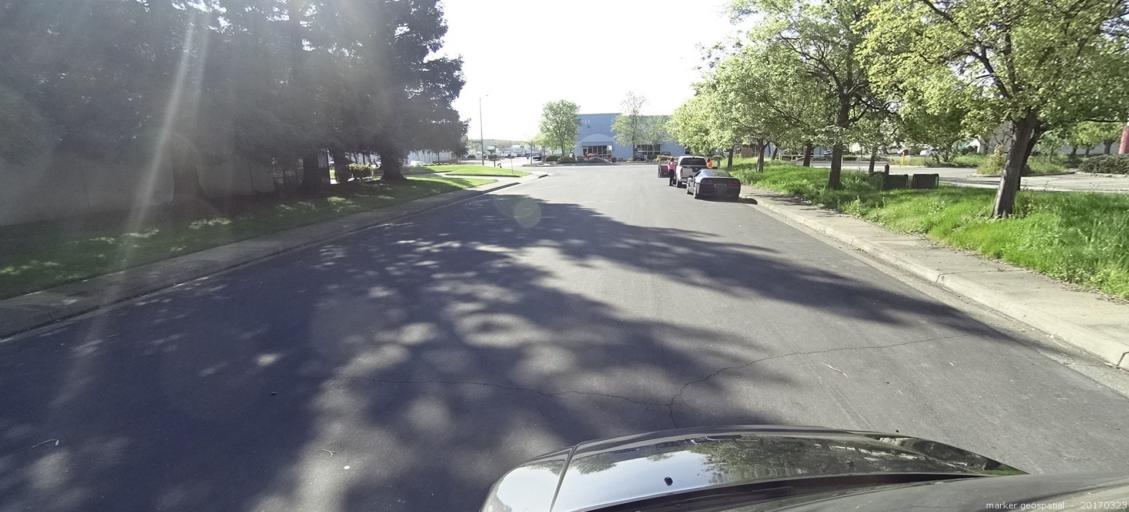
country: US
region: California
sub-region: Sacramento County
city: Florin
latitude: 38.5146
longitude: -121.3839
